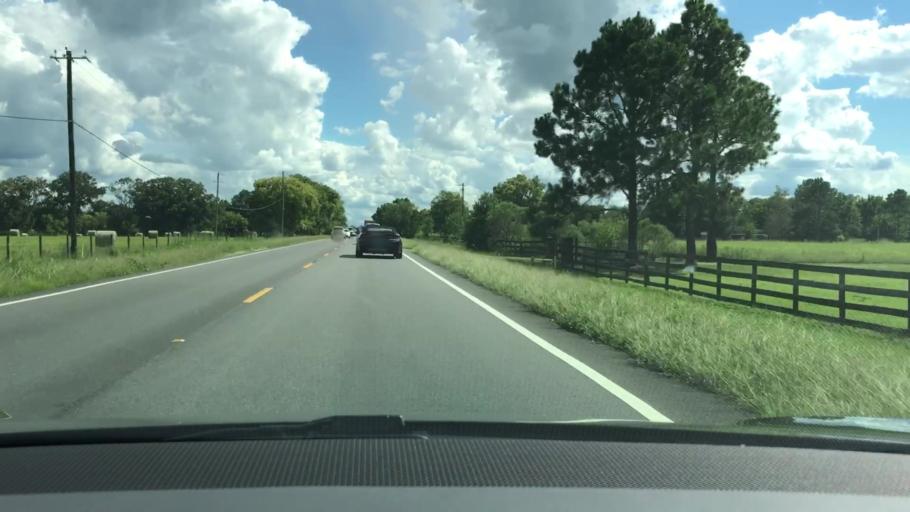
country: US
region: Alabama
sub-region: Montgomery County
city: Pike Road
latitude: 32.3056
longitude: -86.1027
